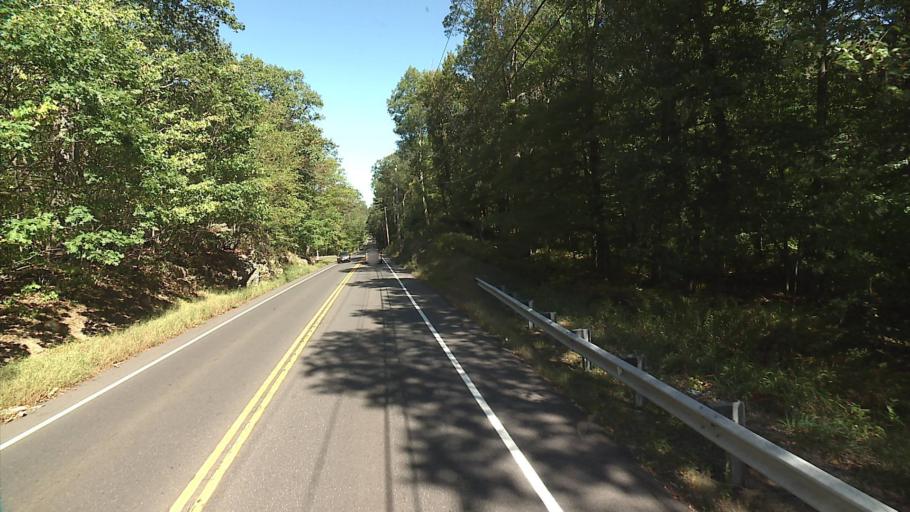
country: US
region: Connecticut
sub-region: New Haven County
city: Prospect
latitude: 41.4553
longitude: -72.9680
